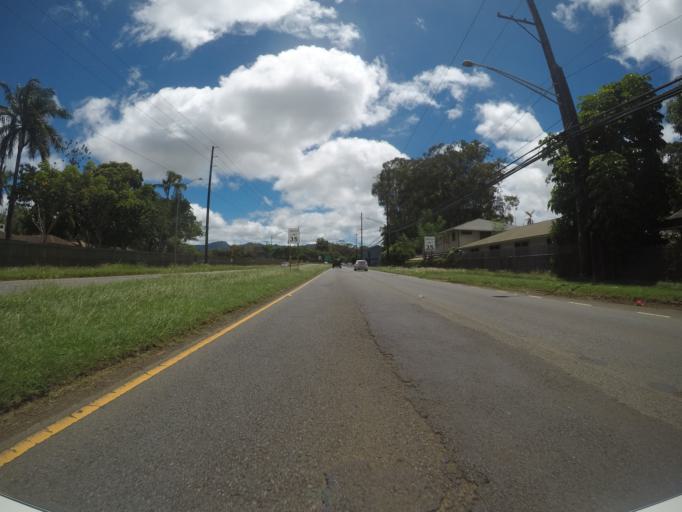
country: US
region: Hawaii
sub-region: Honolulu County
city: Wahiawa
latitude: 21.4893
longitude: -158.0359
